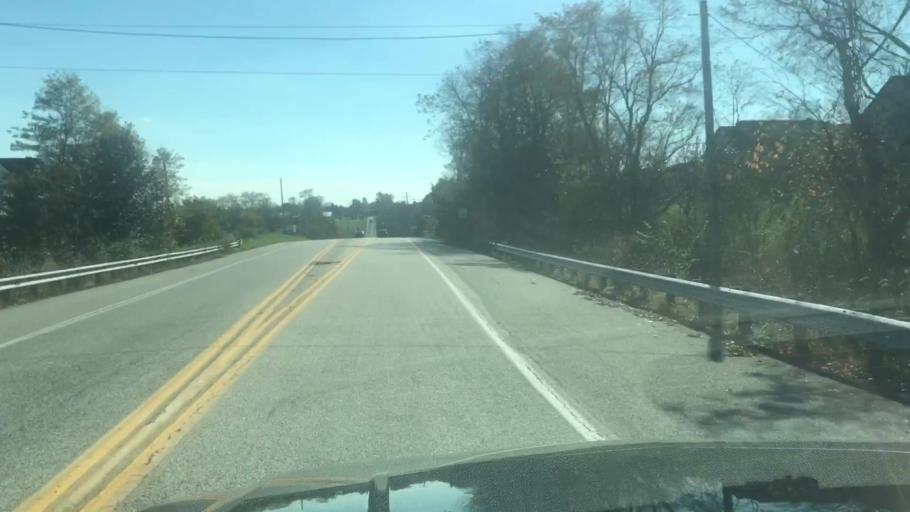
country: US
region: Pennsylvania
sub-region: Cumberland County
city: Enola
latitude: 40.2762
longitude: -76.9867
